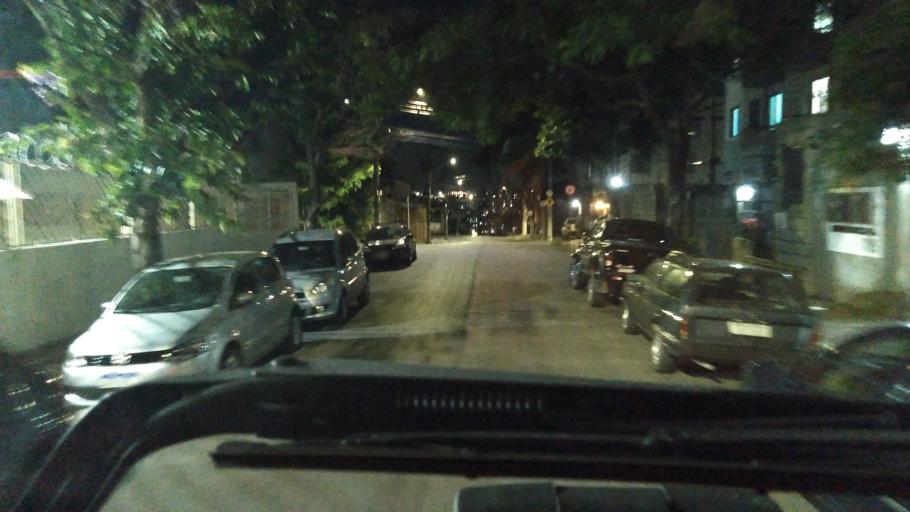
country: BR
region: Minas Gerais
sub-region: Belo Horizonte
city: Belo Horizonte
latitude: -19.9166
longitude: -43.9813
